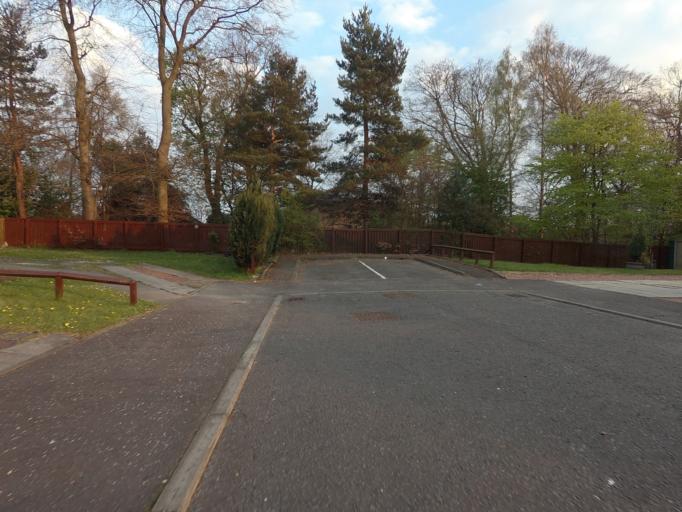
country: GB
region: Scotland
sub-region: West Lothian
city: Livingston
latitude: 55.8972
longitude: -3.5292
